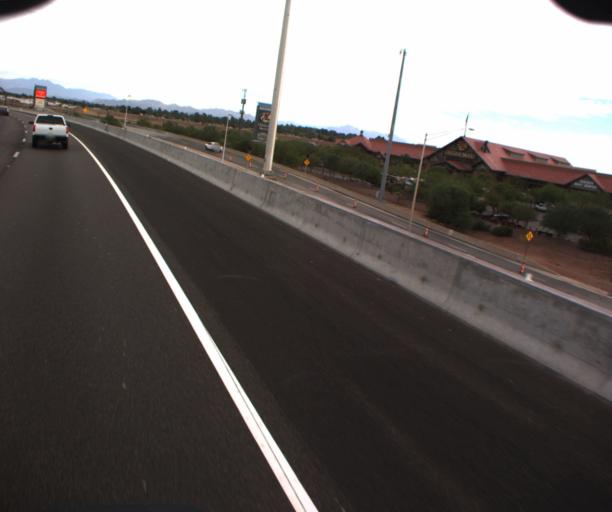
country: US
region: Arizona
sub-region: Maricopa County
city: Tempe
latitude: 33.4373
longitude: -111.8699
